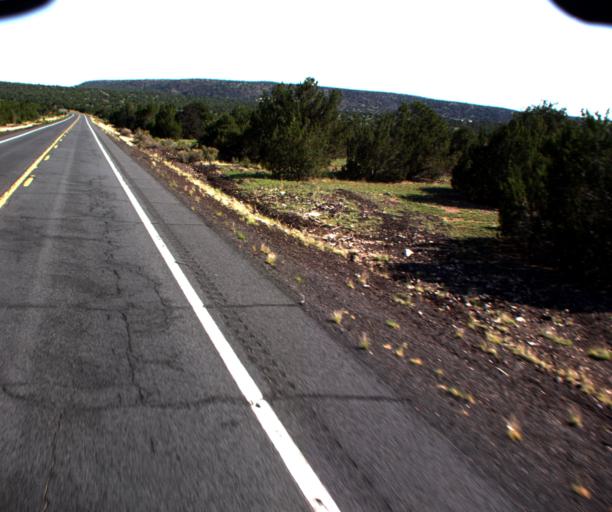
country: US
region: Arizona
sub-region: Coconino County
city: Williams
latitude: 35.4508
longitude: -112.1709
